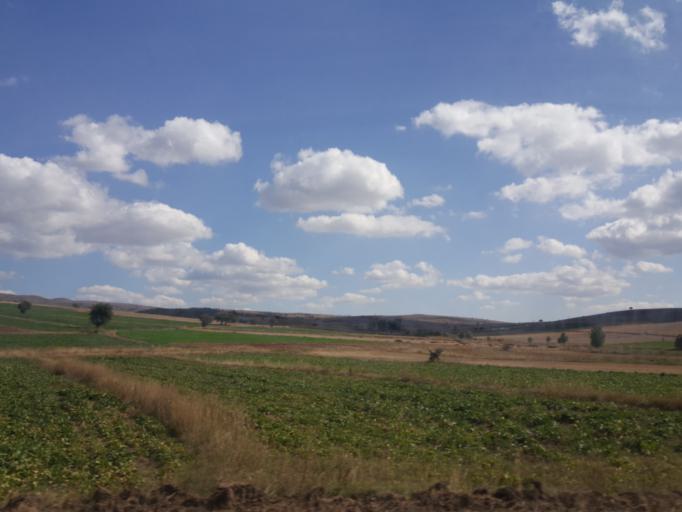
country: TR
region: Tokat
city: Camlibel
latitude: 40.1962
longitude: 36.4639
